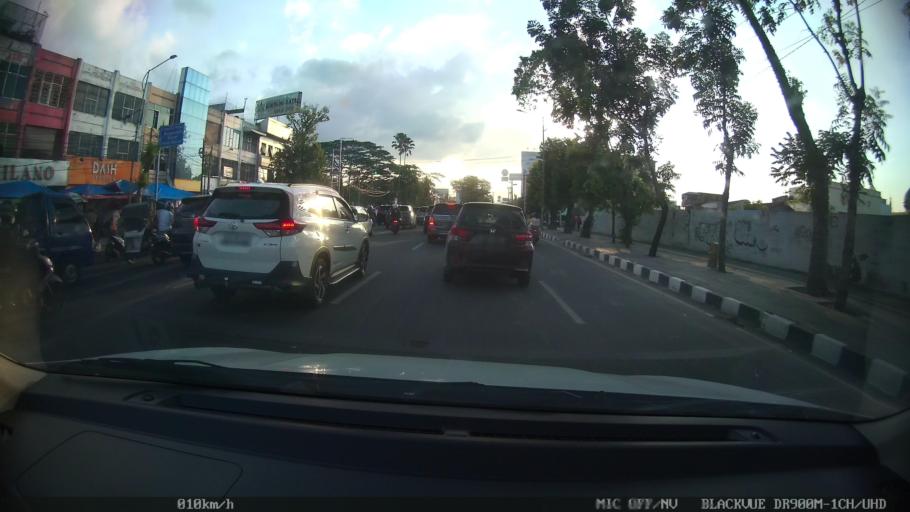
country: ID
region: North Sumatra
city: Medan
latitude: 3.5910
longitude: 98.6622
